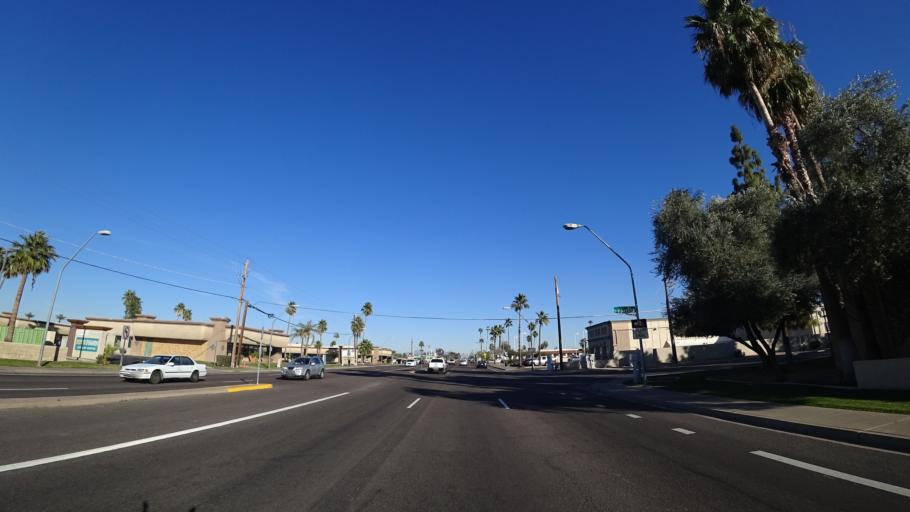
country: US
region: Arizona
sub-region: Maricopa County
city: Mesa
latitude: 33.3932
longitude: -111.8433
